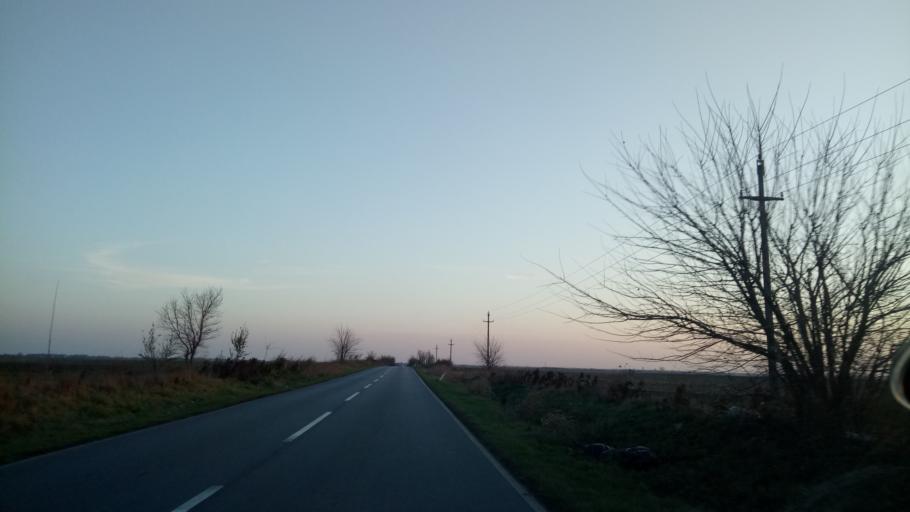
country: RS
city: Surduk
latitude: 45.0514
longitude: 20.3318
